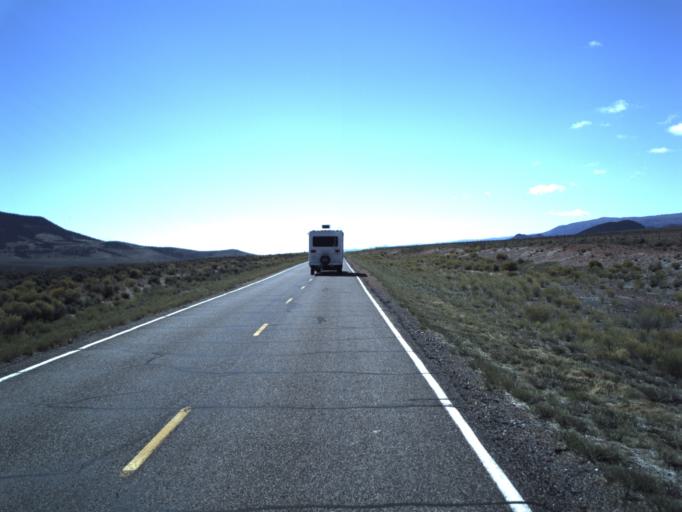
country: US
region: Utah
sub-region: Wayne County
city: Loa
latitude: 38.3941
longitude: -111.9316
